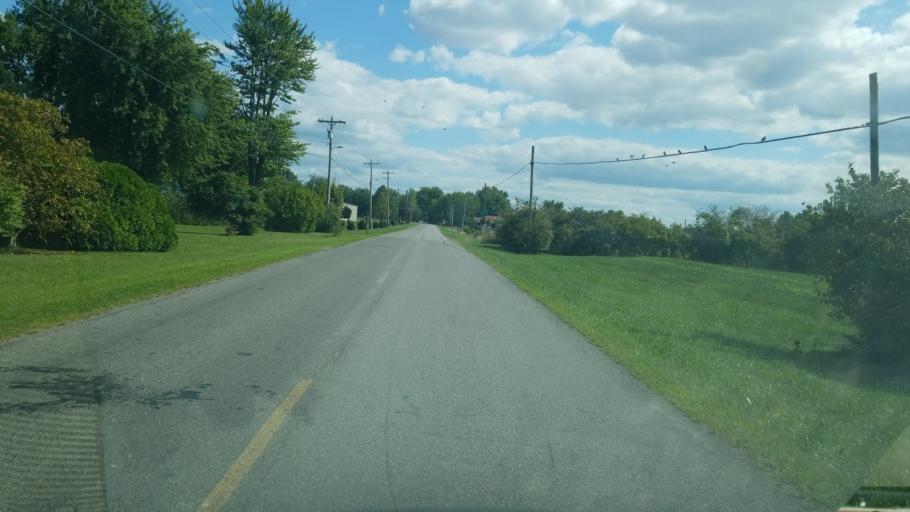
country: US
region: Ohio
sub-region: Logan County
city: Lakeview
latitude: 40.4927
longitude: -83.9296
